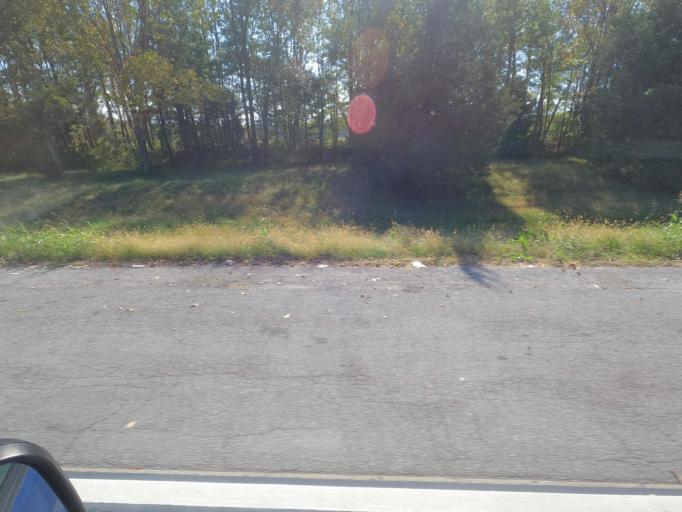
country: US
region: Tennessee
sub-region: Cheatham County
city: Pleasant View
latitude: 36.4481
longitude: -87.0986
